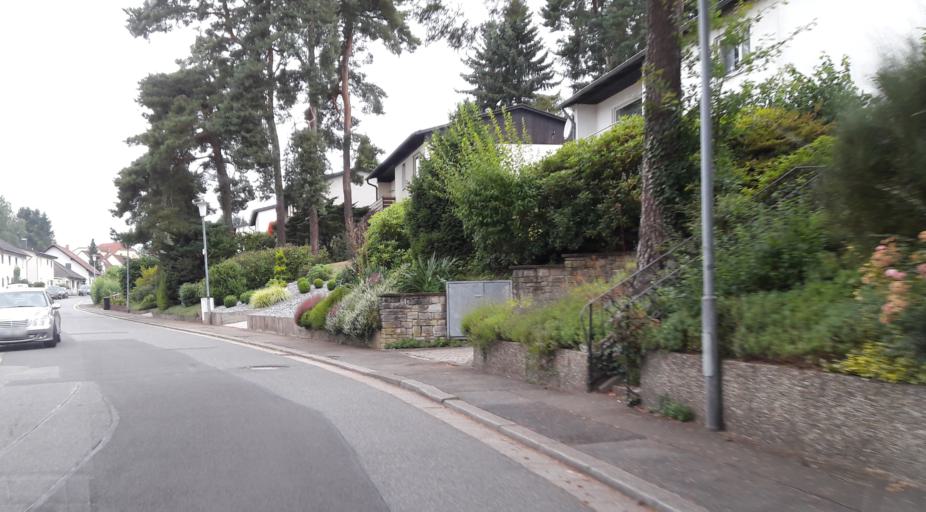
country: DE
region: Saarland
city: Spiesen-Elversberg
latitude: 49.3135
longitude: 7.1421
